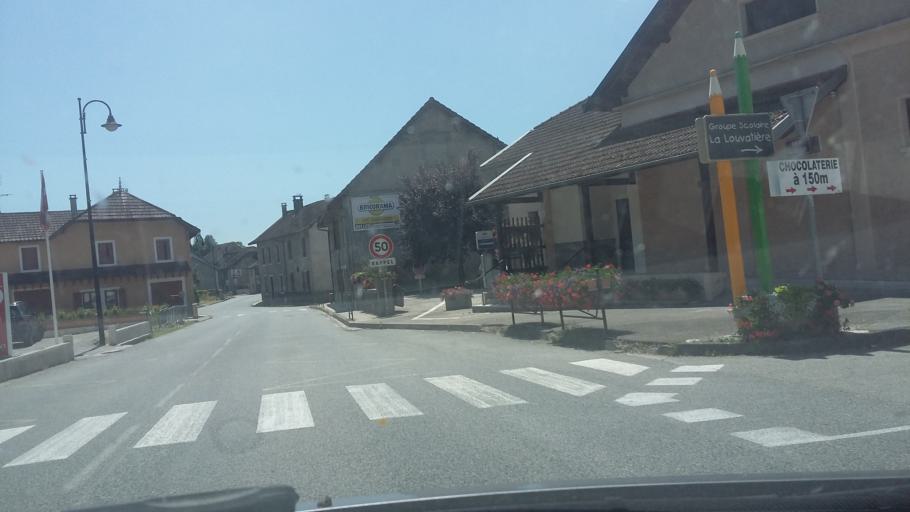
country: FR
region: Rhone-Alpes
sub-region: Departement de l'Ain
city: Belley
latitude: 45.8044
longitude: 5.6822
